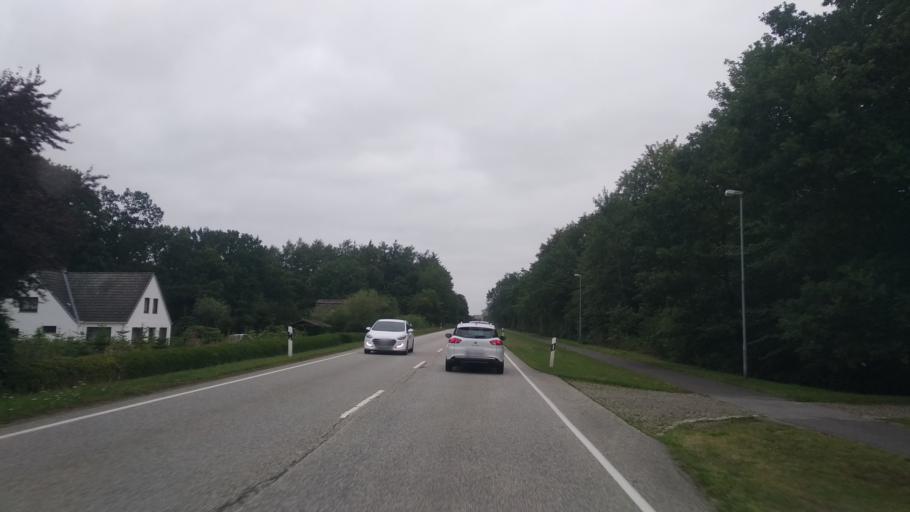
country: DE
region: Schleswig-Holstein
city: Oeversee
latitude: 54.6968
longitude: 9.4337
